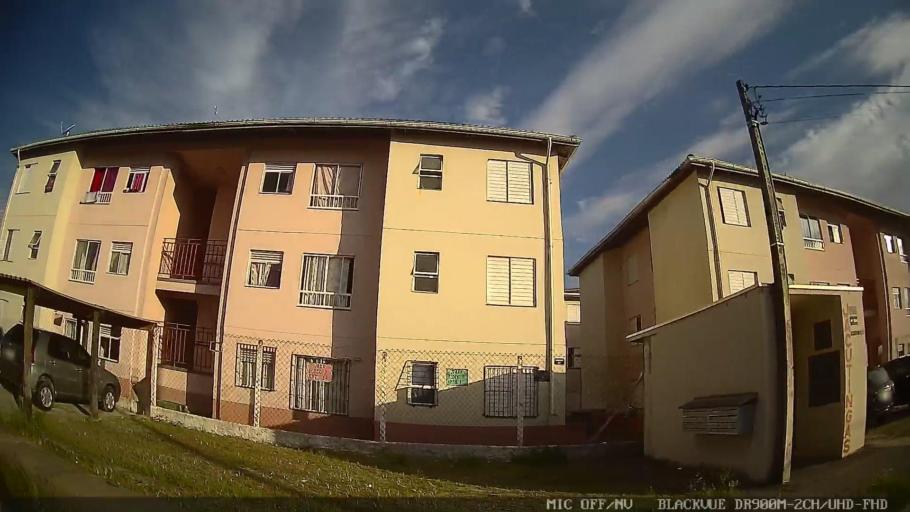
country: BR
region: Sao Paulo
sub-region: Itanhaem
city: Itanhaem
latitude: -24.1503
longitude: -46.7960
